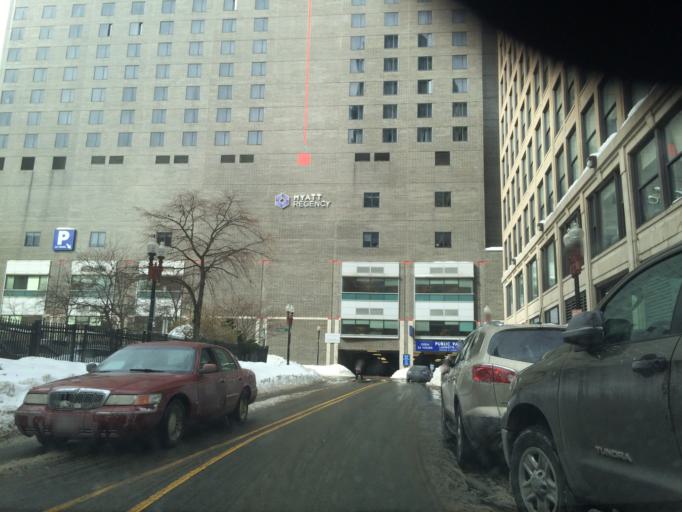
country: US
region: Massachusetts
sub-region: Suffolk County
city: Boston
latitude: 42.3533
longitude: -71.0596
